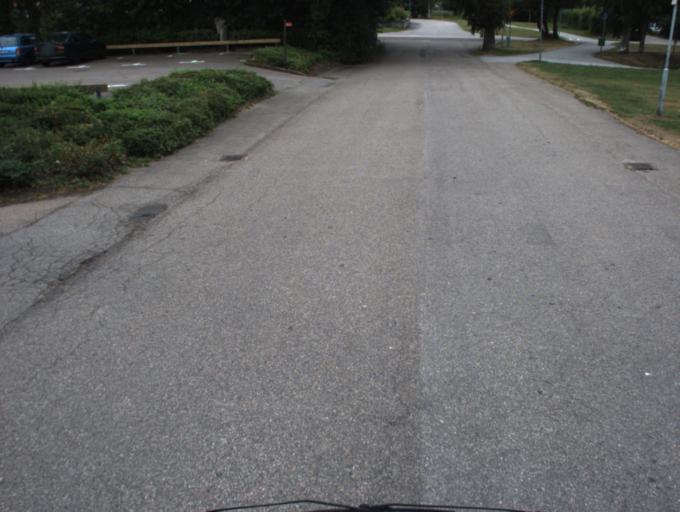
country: SE
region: Skane
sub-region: Helsingborg
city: Morarp
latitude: 56.0588
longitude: 12.8807
